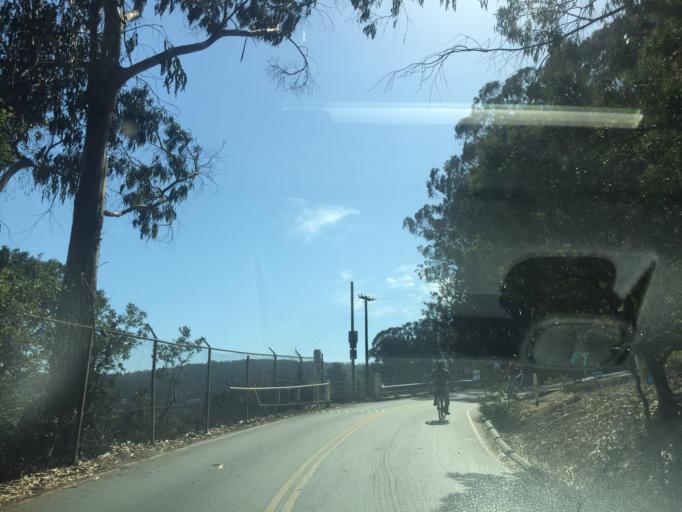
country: US
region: California
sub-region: Marin County
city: Sausalito
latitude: 37.8063
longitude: -122.4700
